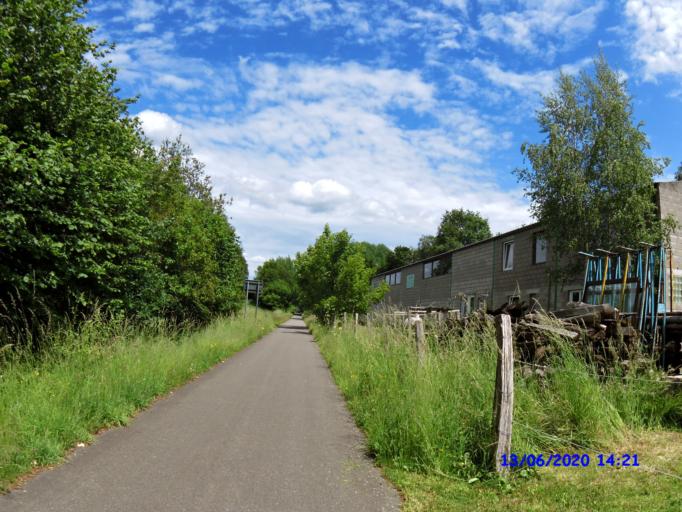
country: BE
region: Wallonia
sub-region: Province de Liege
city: Stavelot
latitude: 50.4090
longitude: 5.9704
